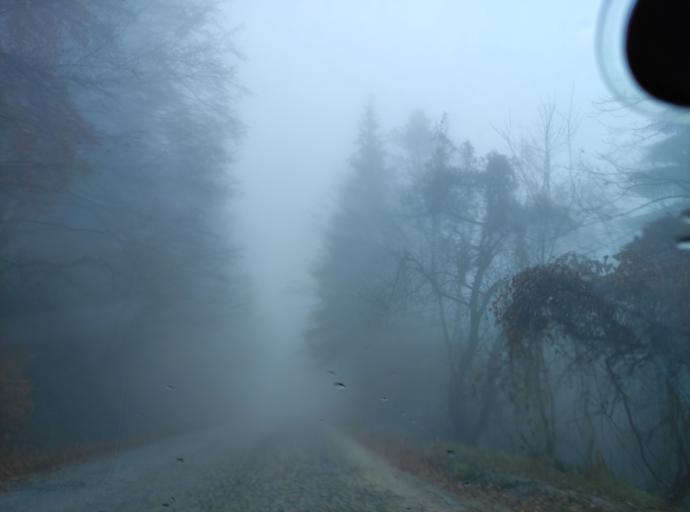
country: BG
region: Sofia-Capital
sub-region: Stolichna Obshtina
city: Sofia
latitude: 42.6165
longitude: 23.2955
